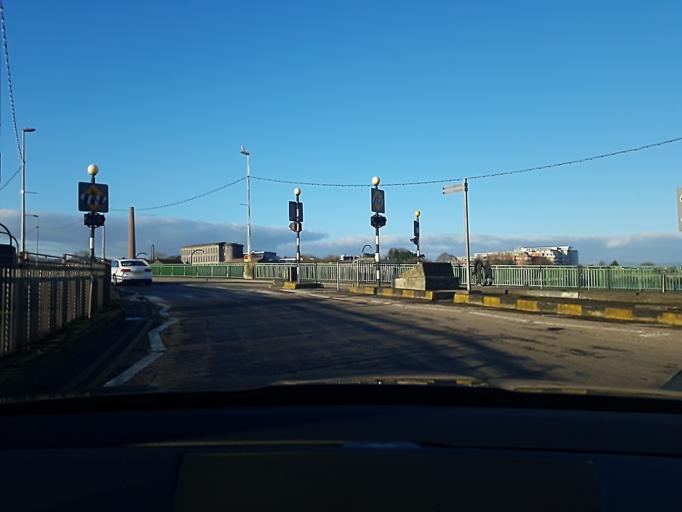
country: IE
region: Munster
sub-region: County Limerick
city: Luimneach
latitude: 52.6614
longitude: -8.6338
